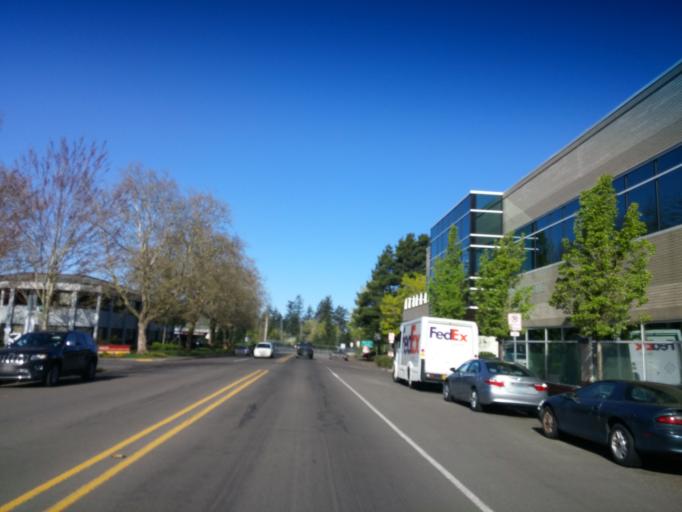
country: US
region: Oregon
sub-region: Washington County
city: West Haven-Sylvan
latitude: 45.5058
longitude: -122.7777
